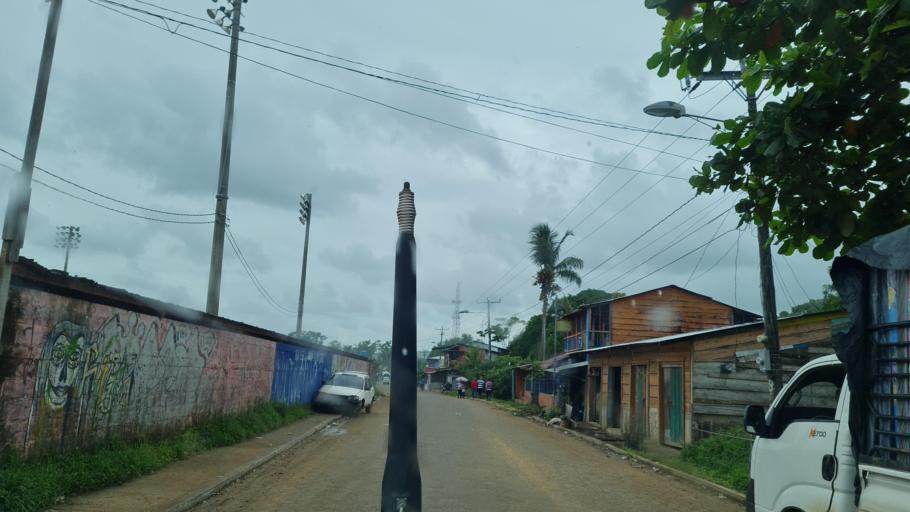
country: NI
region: Atlantico Norte (RAAN)
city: Bonanza
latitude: 13.9238
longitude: -84.3974
